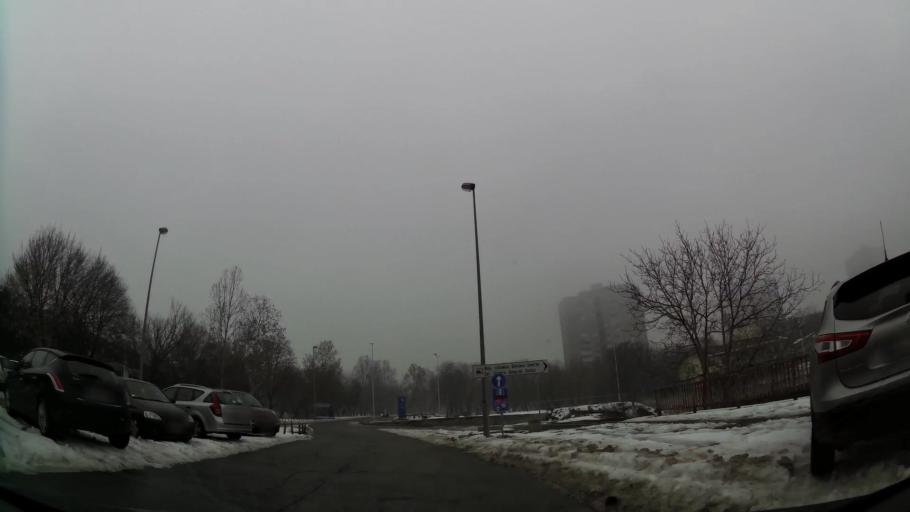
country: RS
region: Central Serbia
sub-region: Belgrade
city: Savski Venac
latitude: 44.7920
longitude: 20.4575
